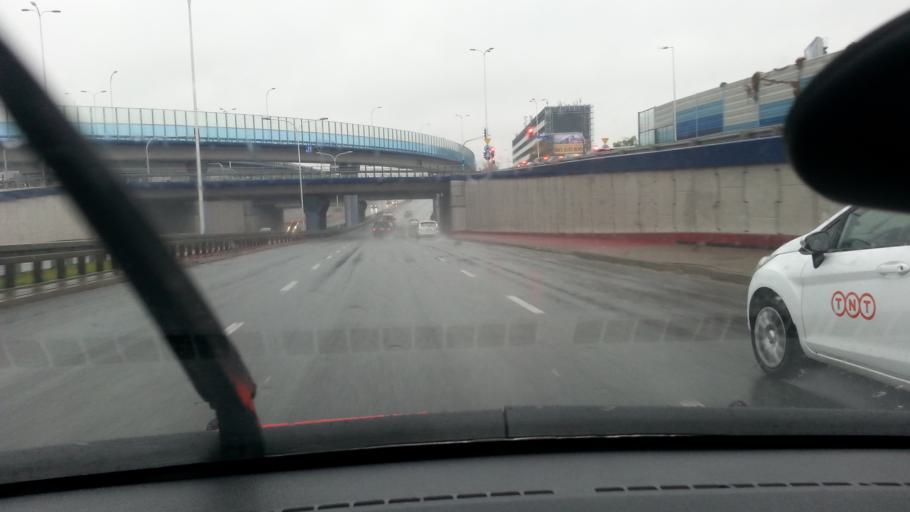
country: PL
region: Masovian Voivodeship
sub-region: Warszawa
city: Wlochy
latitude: 52.1968
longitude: 20.9294
